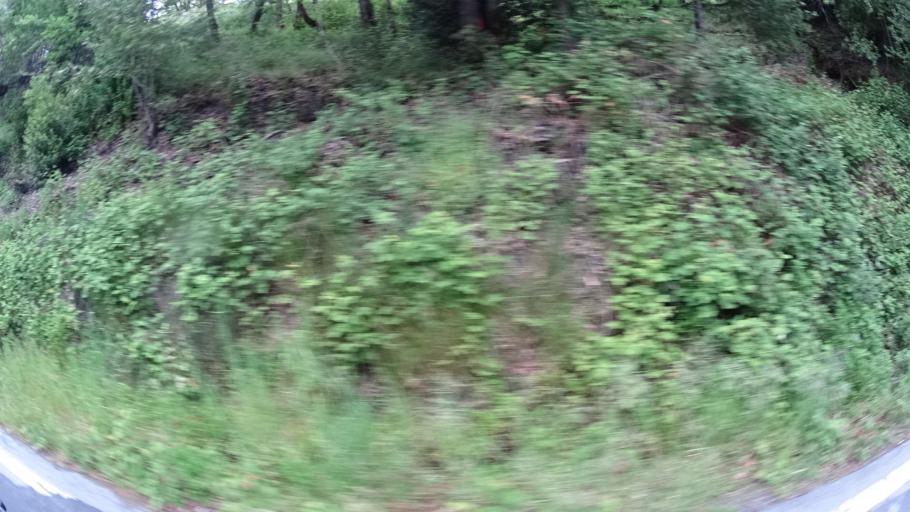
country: US
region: California
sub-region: Humboldt County
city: Willow Creek
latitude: 41.1901
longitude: -123.7120
